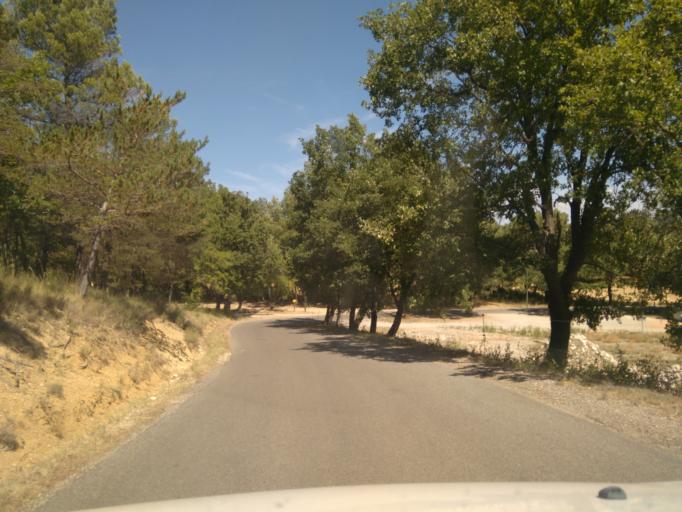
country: FR
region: Provence-Alpes-Cote d'Azur
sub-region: Departement du Var
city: Regusse
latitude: 43.7214
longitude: 6.0642
